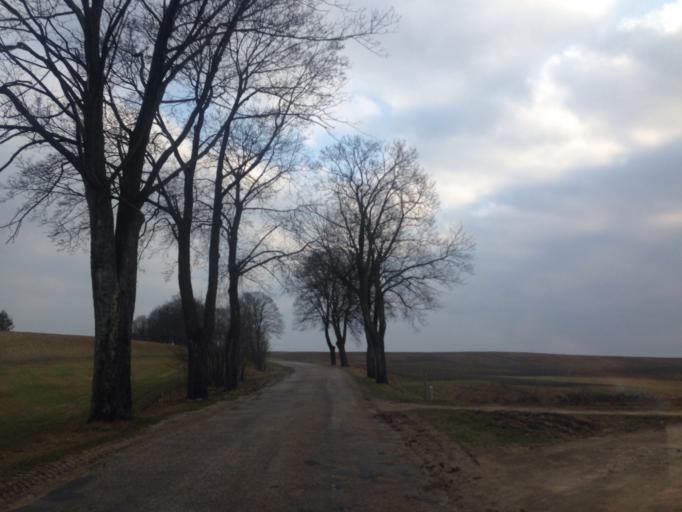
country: PL
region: Kujawsko-Pomorskie
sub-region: Powiat brodnicki
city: Brzozie
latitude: 53.3364
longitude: 19.7140
